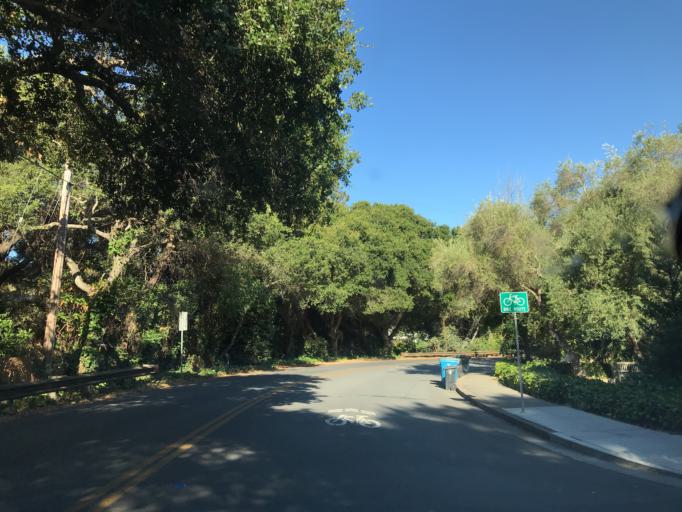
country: US
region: California
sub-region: San Mateo County
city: East Palo Alto
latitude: 37.4569
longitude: -122.1471
